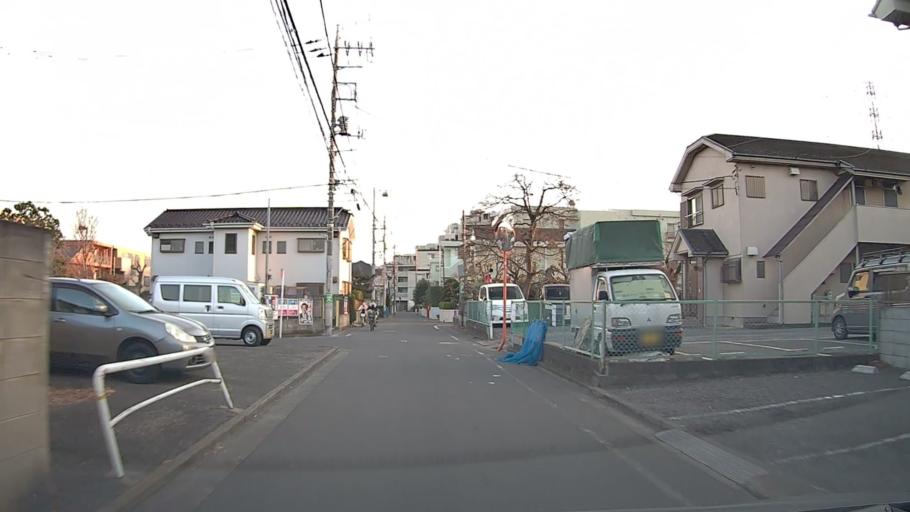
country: JP
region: Tokyo
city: Musashino
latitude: 35.7336
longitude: 139.5801
